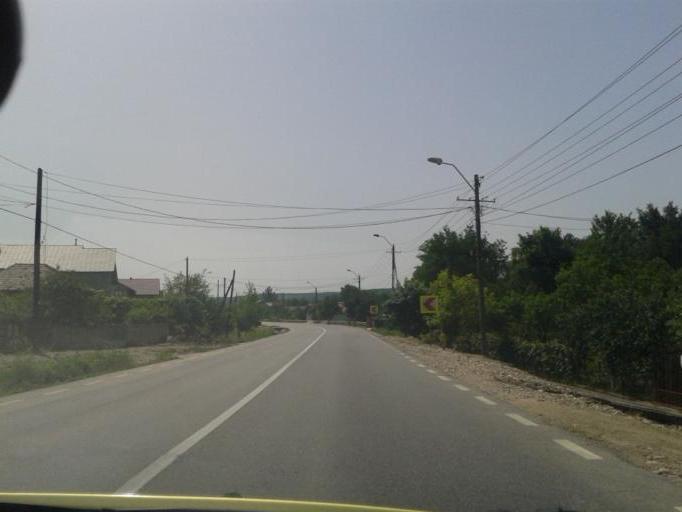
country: RO
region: Arges
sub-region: Comuna Babana
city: Babana
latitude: 44.9000
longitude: 24.7352
